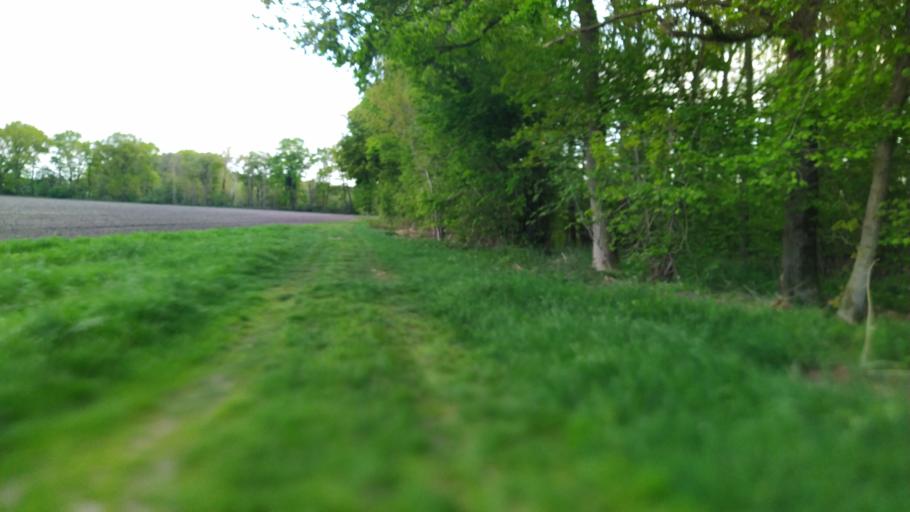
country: DE
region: Lower Saxony
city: Farven
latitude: 53.4330
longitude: 9.3363
